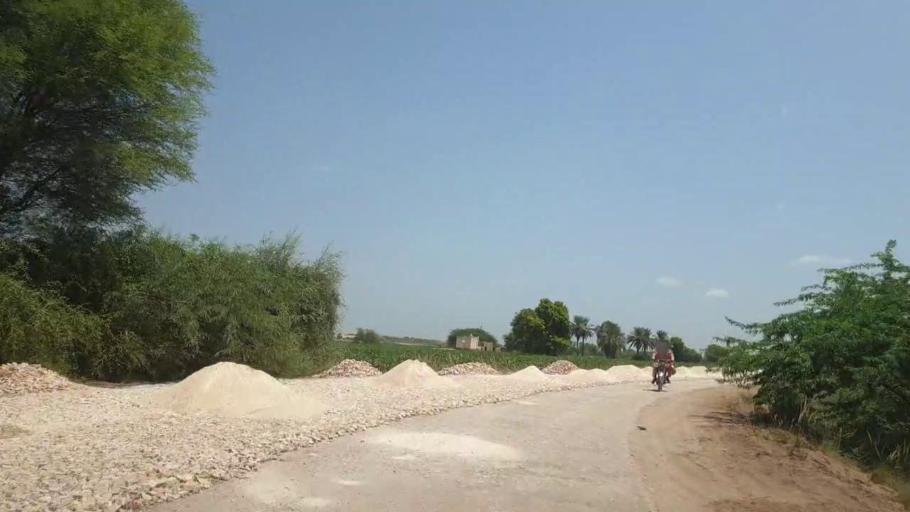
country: PK
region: Sindh
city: Pano Aqil
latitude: 27.6660
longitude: 69.1765
